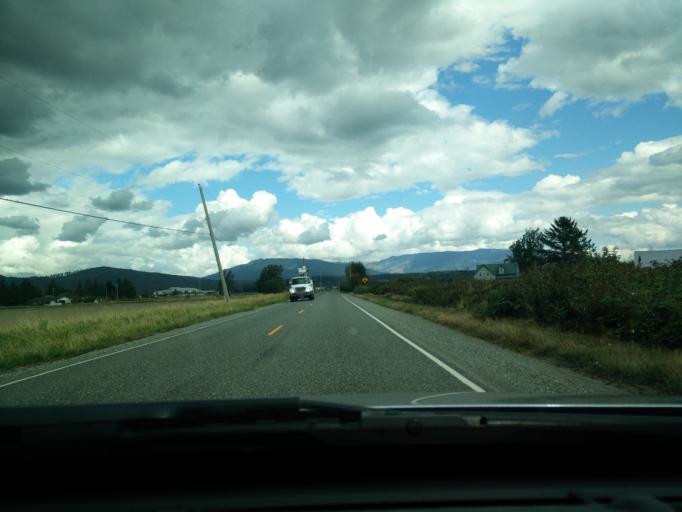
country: US
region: Washington
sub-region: Skagit County
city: Burlington
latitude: 48.5560
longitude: -122.4474
